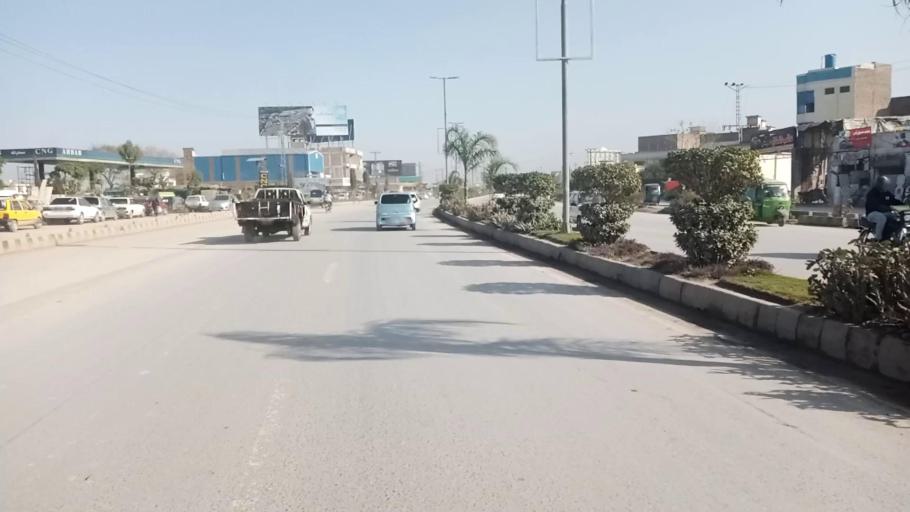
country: PK
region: Khyber Pakhtunkhwa
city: Peshawar
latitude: 34.0335
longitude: 71.6030
